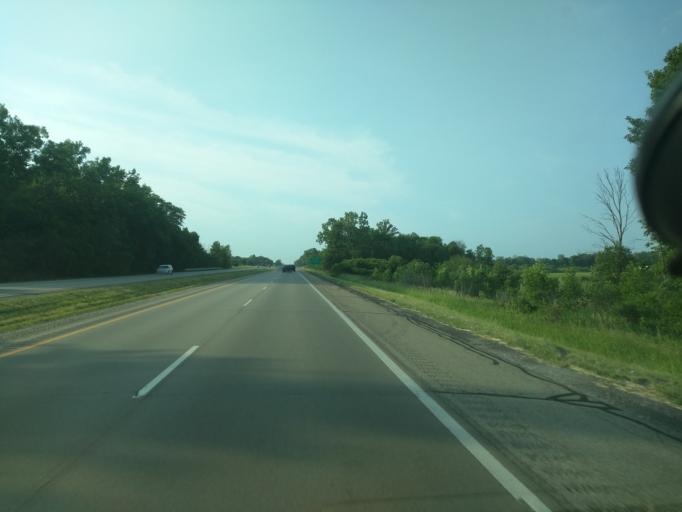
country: US
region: Michigan
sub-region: Ingham County
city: Leslie
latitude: 42.3572
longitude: -84.4288
